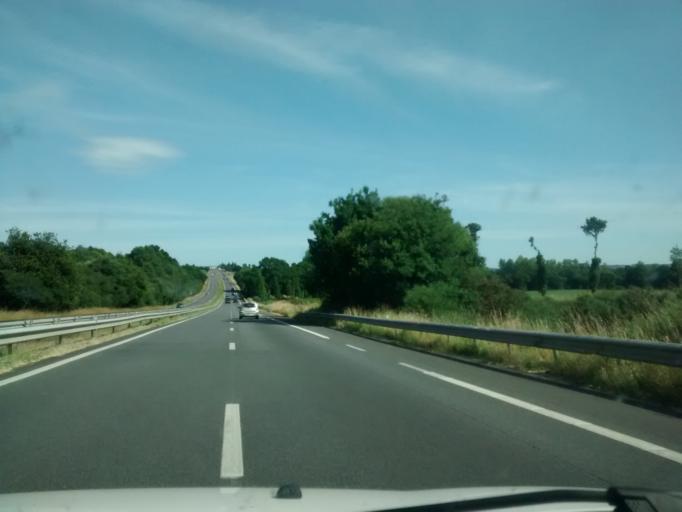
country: FR
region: Brittany
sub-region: Departement des Cotes-d'Armor
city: Sevignac
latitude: 48.3624
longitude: -2.3211
